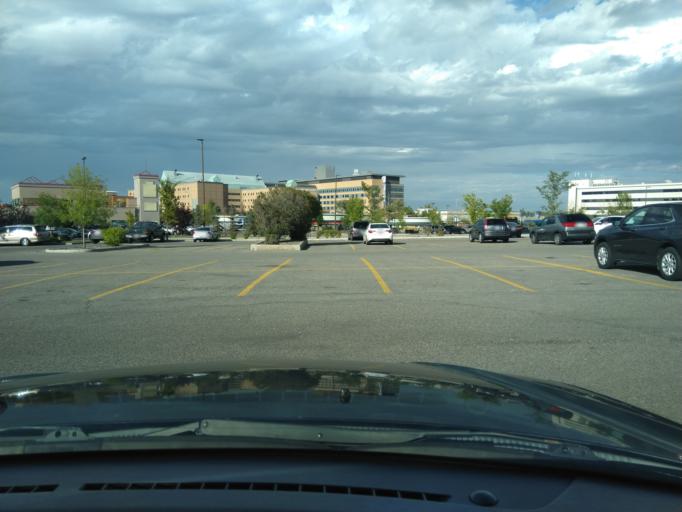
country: CA
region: Alberta
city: Calgary
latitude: 51.0759
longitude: -113.9861
